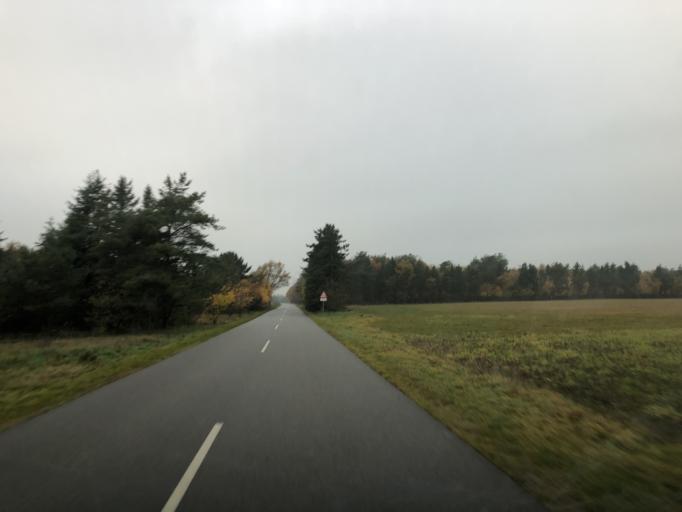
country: DK
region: Central Jutland
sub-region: Herning Kommune
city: Sunds
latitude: 56.2223
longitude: 8.9328
